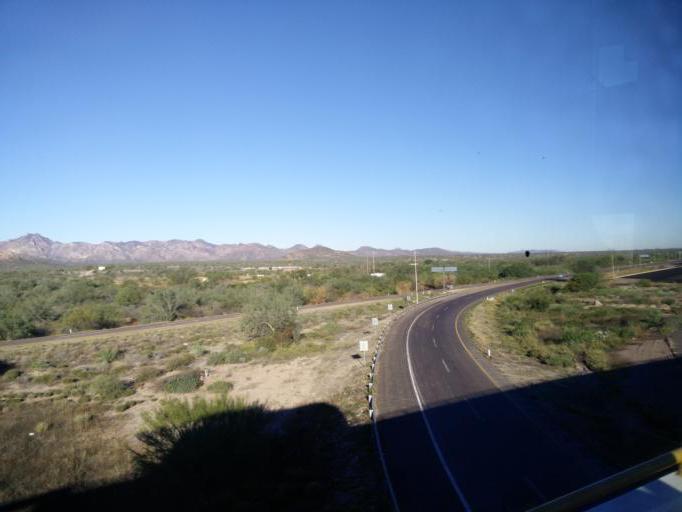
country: MX
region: Sonora
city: Heroica Guaymas
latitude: 28.0389
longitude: -110.9377
